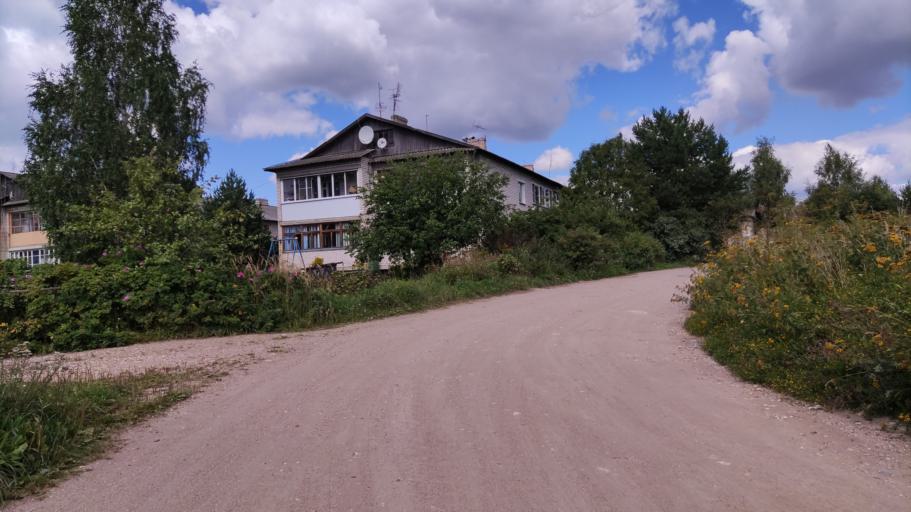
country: RU
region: Tverskaya
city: Rzhev
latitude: 56.2375
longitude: 34.3224
